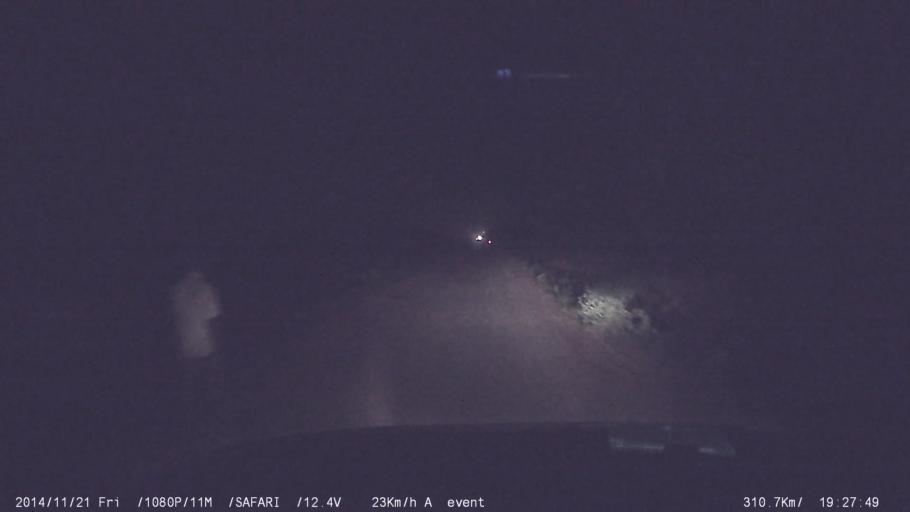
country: IN
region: Tamil Nadu
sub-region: Kancheepuram
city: Singapperumalkovil
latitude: 12.7987
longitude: 79.9958
